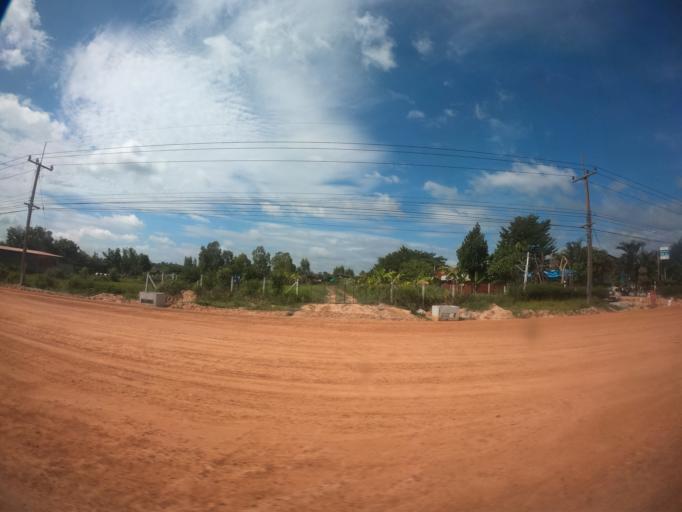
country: TH
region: Surin
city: Kap Choeng
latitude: 14.4564
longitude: 103.6768
